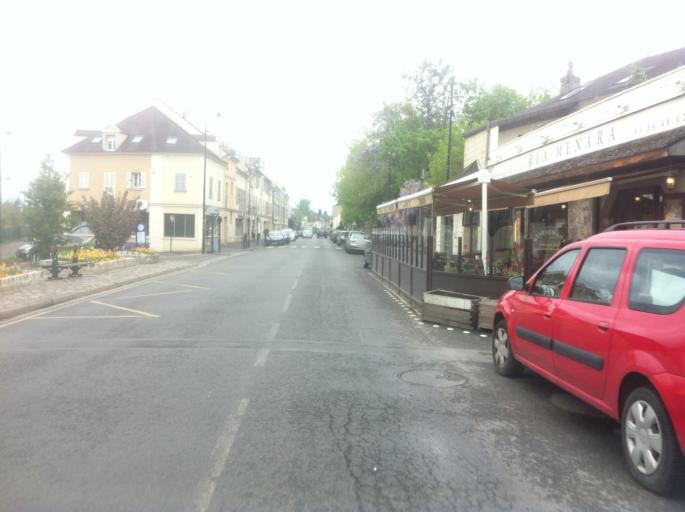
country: FR
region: Ile-de-France
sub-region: Departement du Val-d'Oise
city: Auvers-sur-Oise
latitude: 49.0708
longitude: 2.1754
